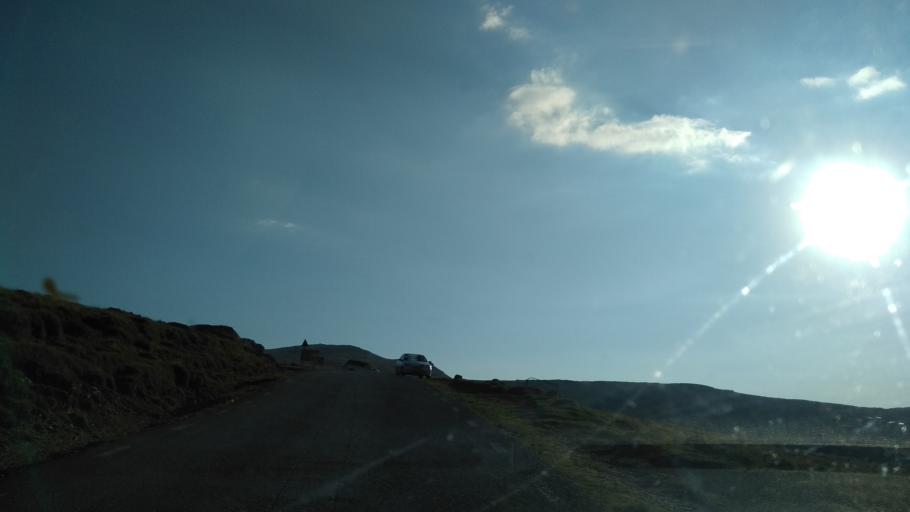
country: RO
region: Prahova
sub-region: Oras Busteni
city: Busteni
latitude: 45.3834
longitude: 25.4744
